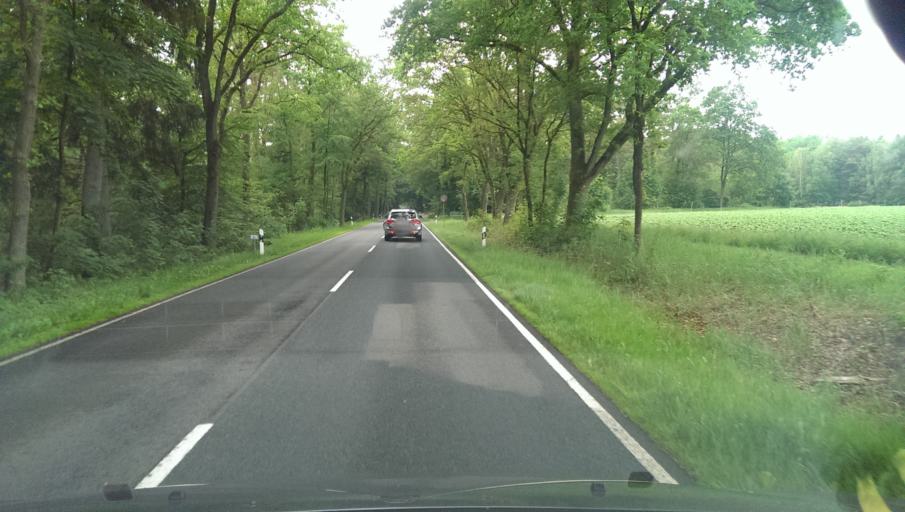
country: DE
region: Lower Saxony
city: Fassberg
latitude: 52.8703
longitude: 10.2305
